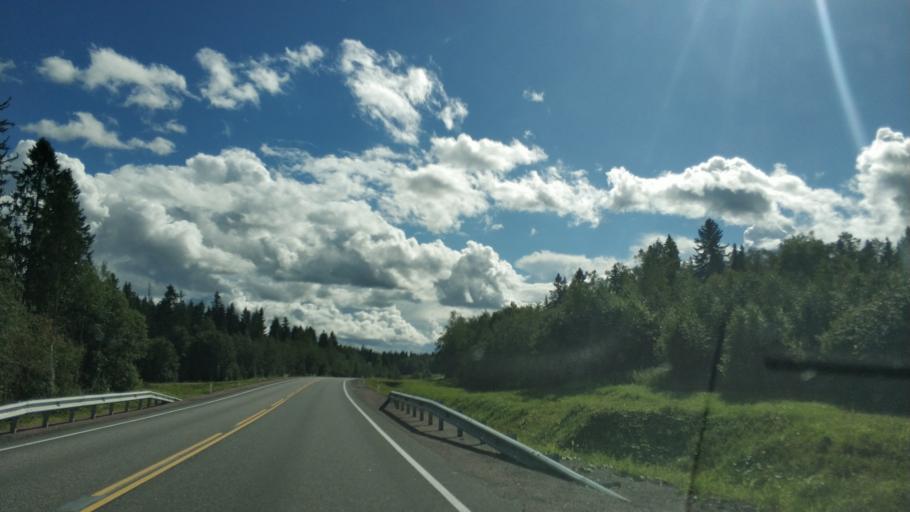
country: RU
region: Republic of Karelia
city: Ruskeala
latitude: 61.8916
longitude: 30.6427
